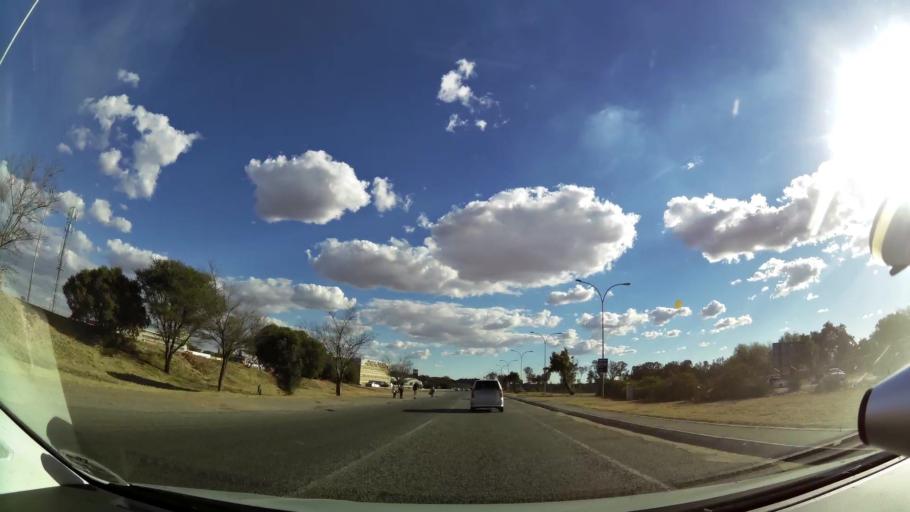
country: ZA
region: North-West
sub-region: Dr Kenneth Kaunda District Municipality
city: Klerksdorp
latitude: -26.8613
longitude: 26.6643
